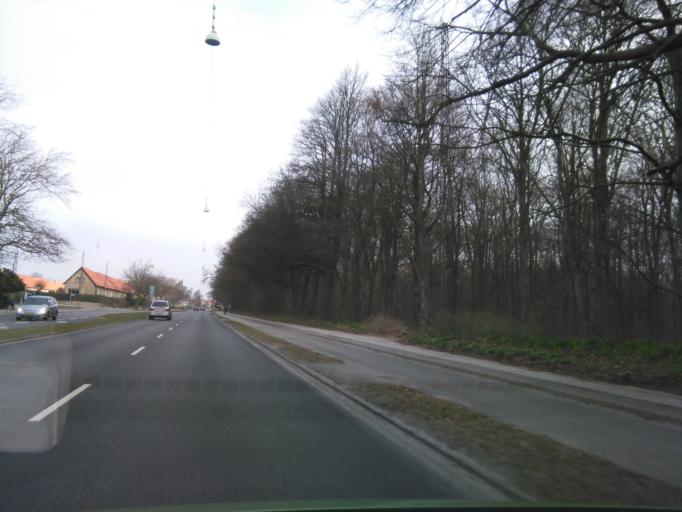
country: DK
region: Central Jutland
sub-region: Arhus Kommune
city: Arhus
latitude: 56.1800
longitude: 10.2183
